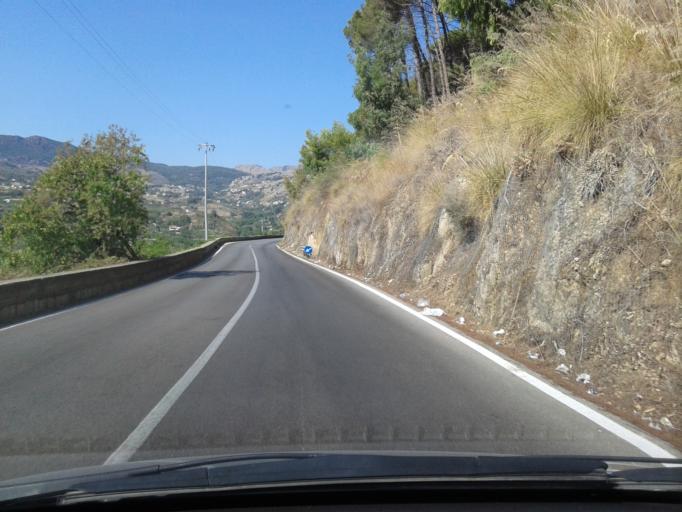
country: IT
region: Sicily
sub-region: Palermo
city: Pioppo
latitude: 38.0534
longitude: 13.2481
